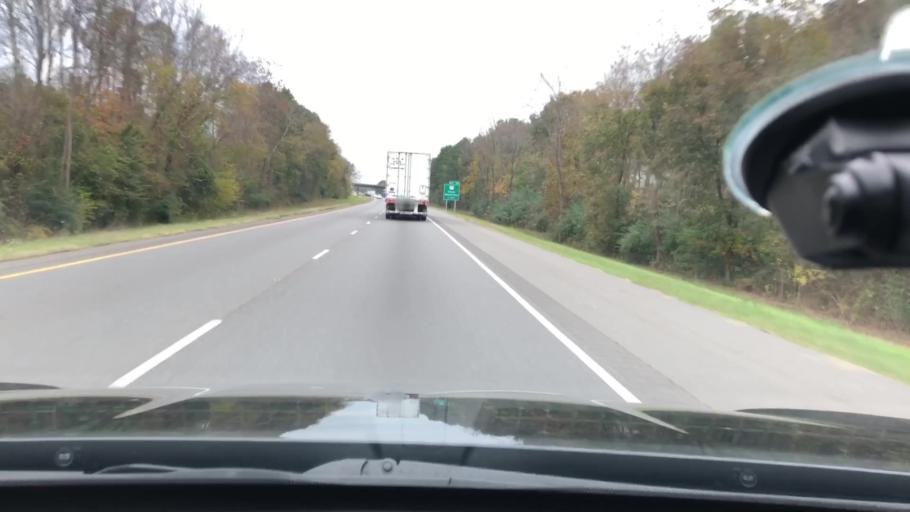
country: US
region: Arkansas
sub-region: Hempstead County
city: Hope
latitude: 33.6665
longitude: -93.6319
